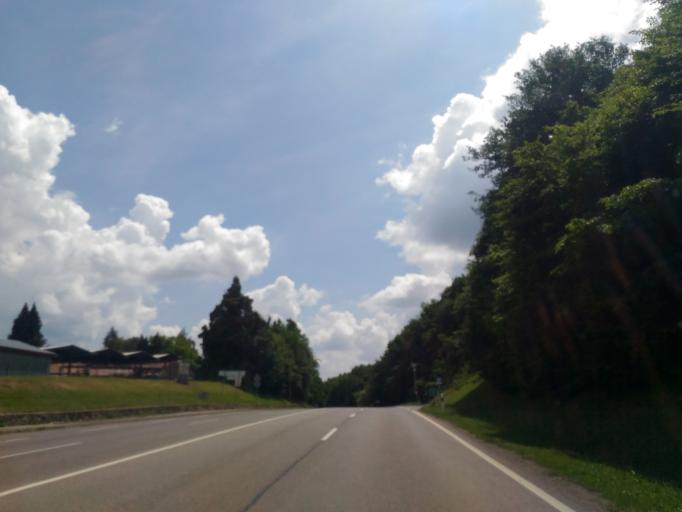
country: HU
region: Baranya
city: Pecs
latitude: 46.1376
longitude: 18.2505
